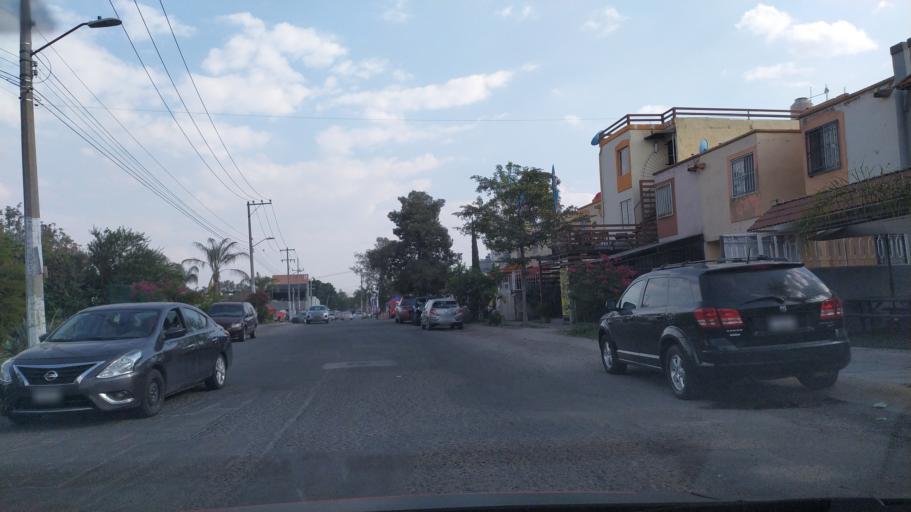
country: MX
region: Jalisco
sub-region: Tlajomulco de Zuniga
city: Palomar
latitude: 20.6264
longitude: -103.4655
